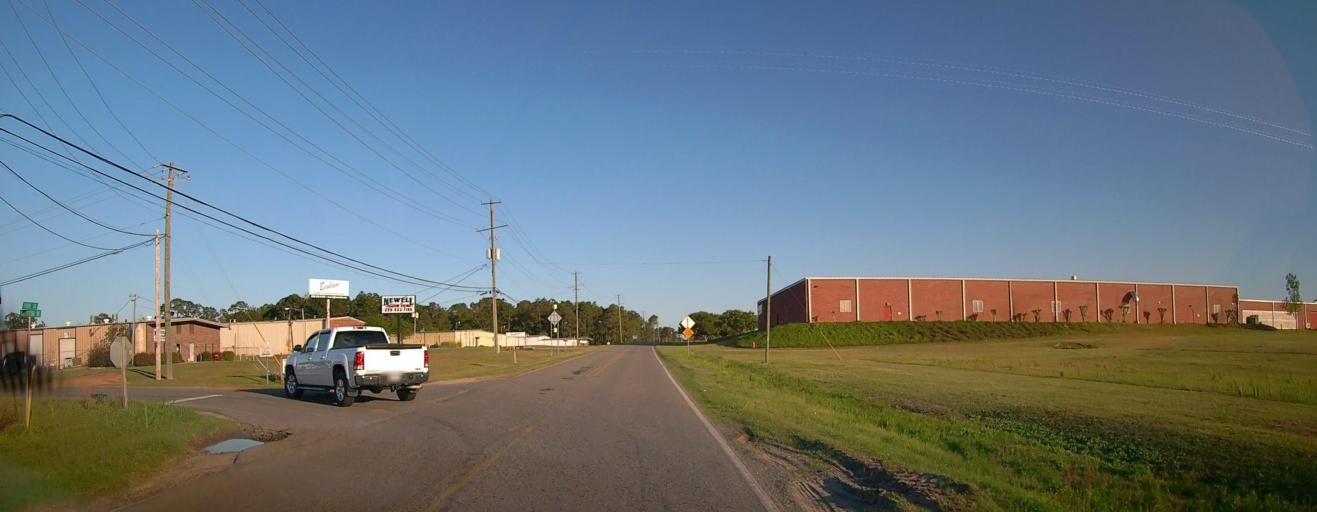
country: US
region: Georgia
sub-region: Ben Hill County
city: Fitzgerald
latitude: 31.6971
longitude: -83.2384
